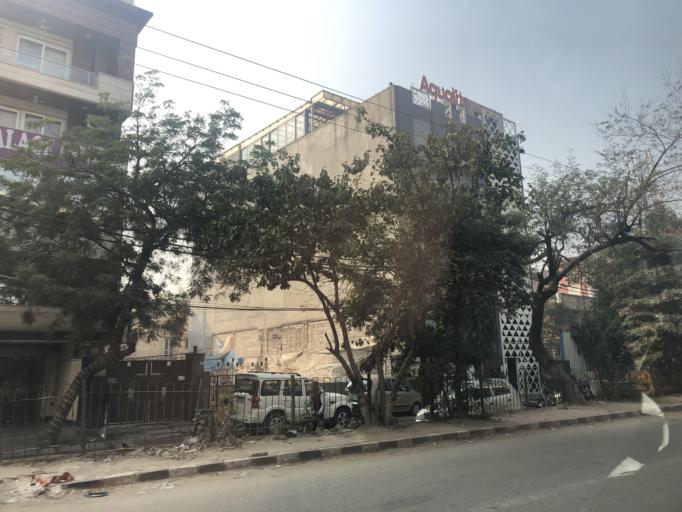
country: IN
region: NCT
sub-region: West Delhi
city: Nangloi Jat
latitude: 28.6788
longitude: 77.1000
